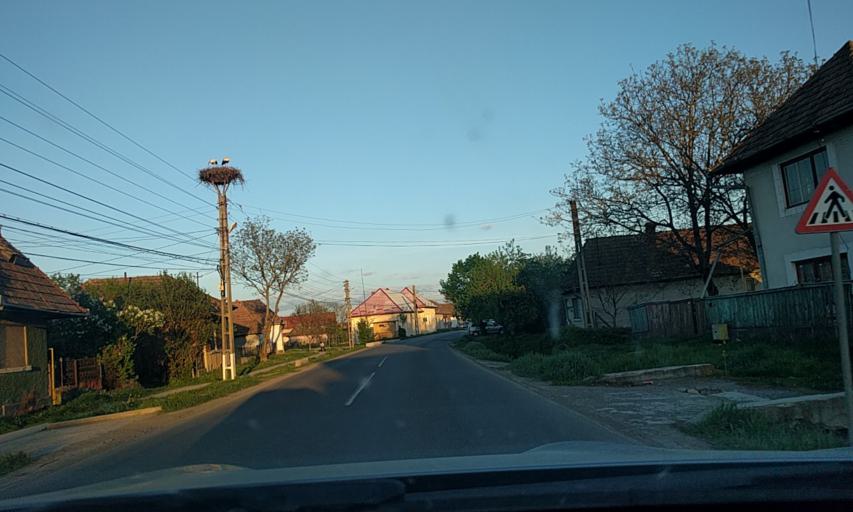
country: RO
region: Mures
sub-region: Comuna Craciunesti
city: Craciunesti
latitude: 46.4797
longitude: 24.5946
